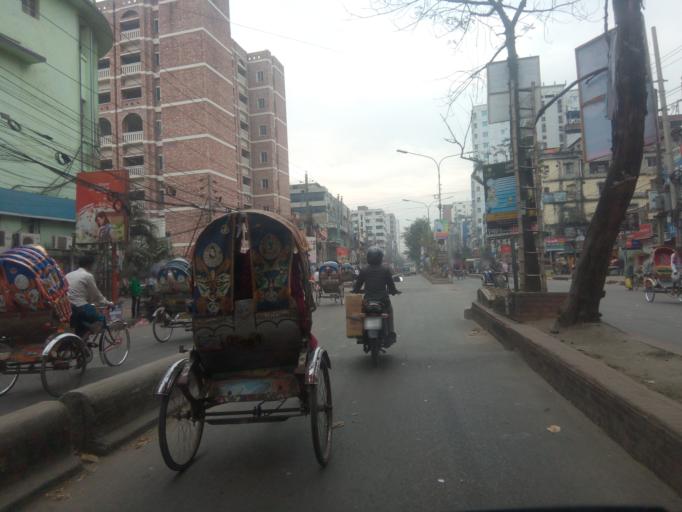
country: BD
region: Dhaka
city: Narayanganj
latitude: 23.6194
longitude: 90.5012
